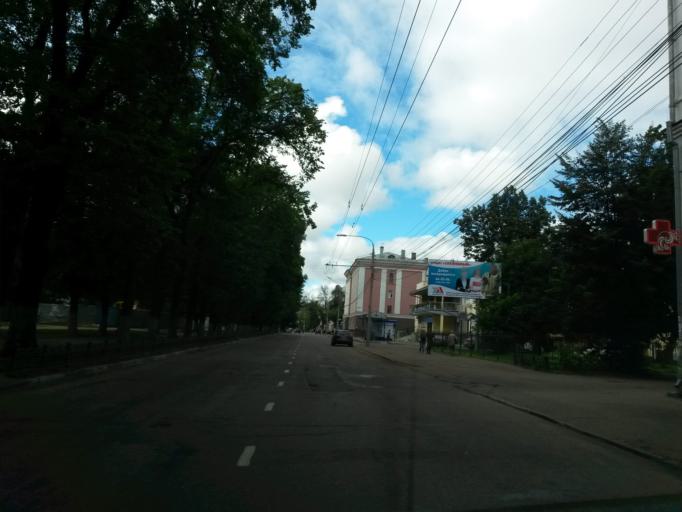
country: RU
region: Jaroslavl
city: Yaroslavl
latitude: 57.6417
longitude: 39.8781
